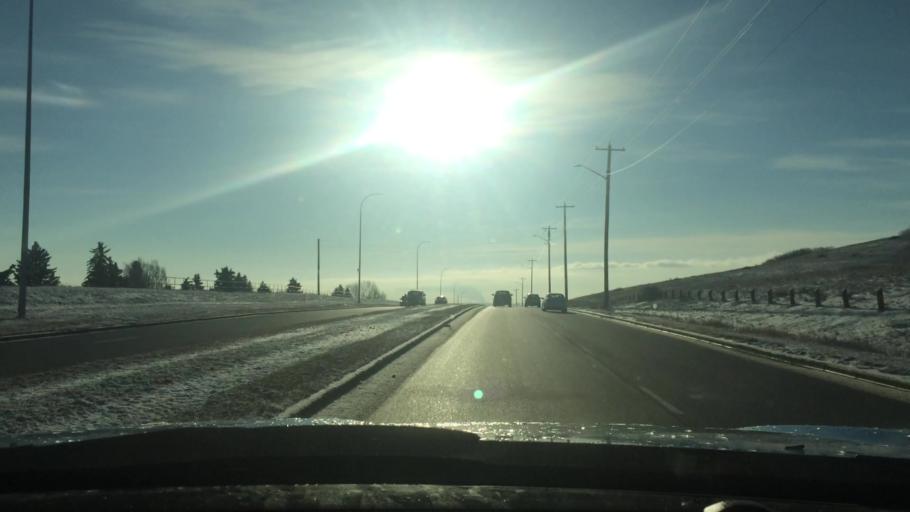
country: CA
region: Alberta
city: Calgary
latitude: 51.1209
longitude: -114.0913
